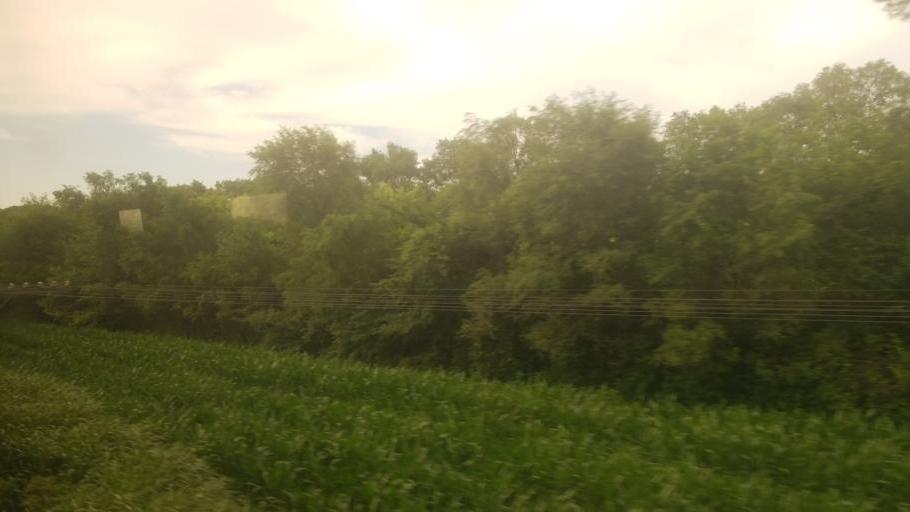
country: US
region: Kansas
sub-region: Shawnee County
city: Topeka
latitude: 39.0547
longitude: -95.5978
